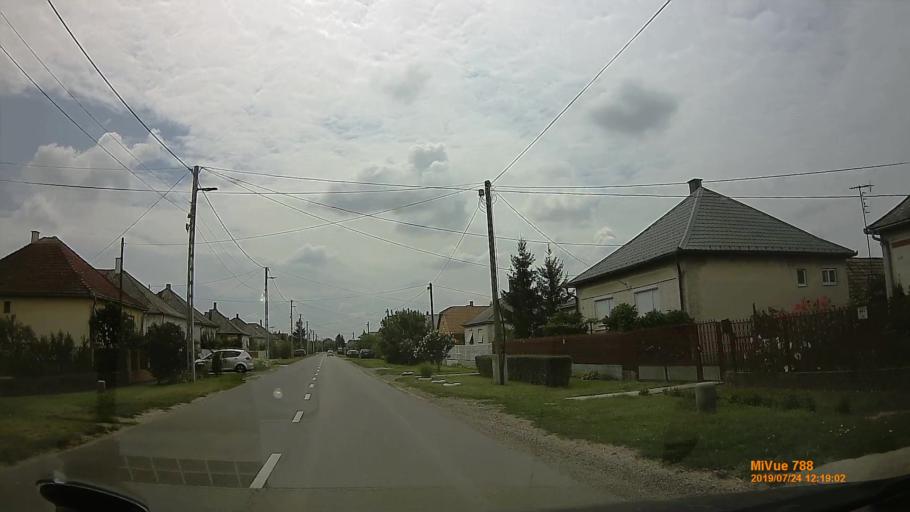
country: HU
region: Szabolcs-Szatmar-Bereg
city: Vasarosnameny
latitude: 48.1444
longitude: 22.3452
